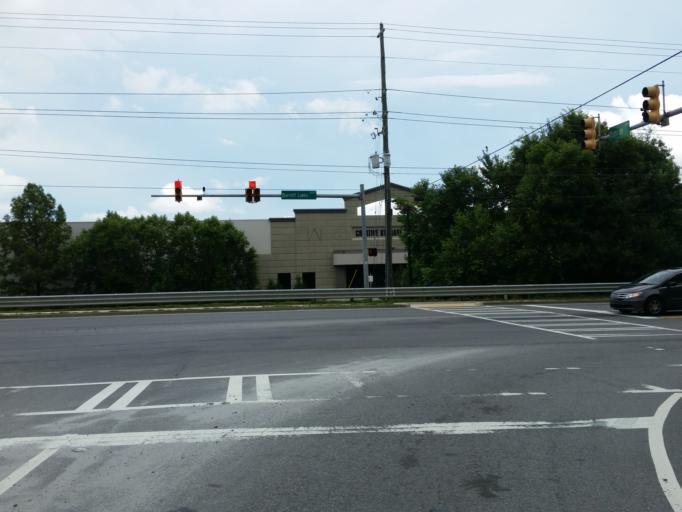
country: US
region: Georgia
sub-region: Cobb County
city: Kennesaw
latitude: 34.0173
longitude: -84.5757
